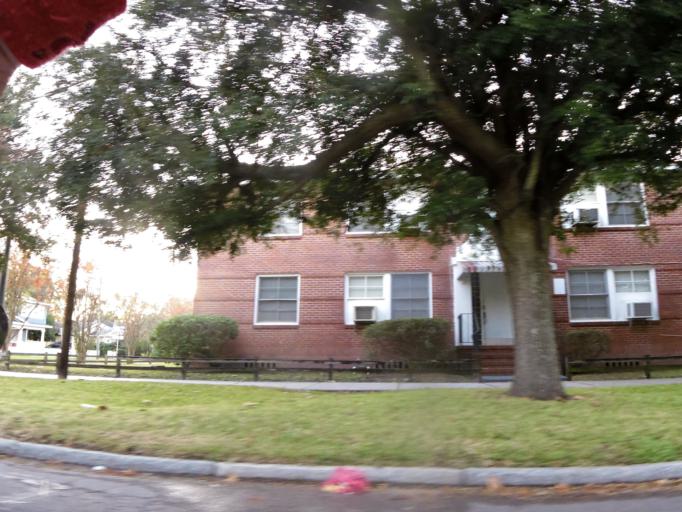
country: US
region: Florida
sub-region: Duval County
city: Jacksonville
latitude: 30.3143
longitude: -81.6891
